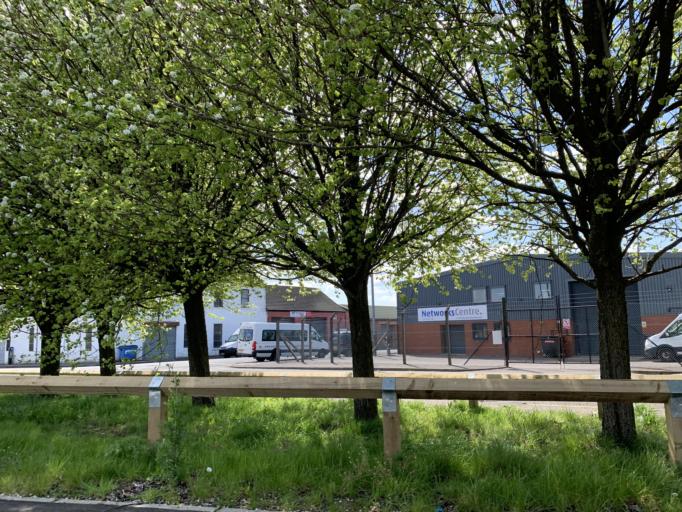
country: GB
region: Scotland
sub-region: Glasgow City
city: Glasgow
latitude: 55.8721
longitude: -4.2508
